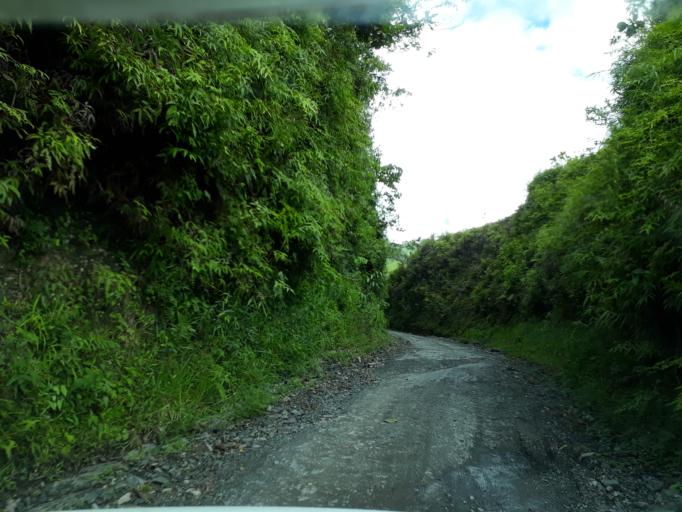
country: CO
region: Boyaca
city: Quipama
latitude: 5.4348
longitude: -74.1859
